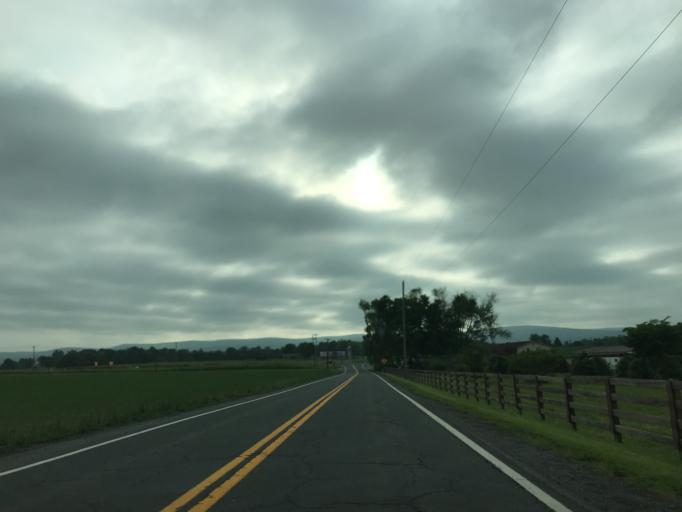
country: US
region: Maryland
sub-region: Frederick County
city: Walkersville
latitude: 39.4815
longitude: -77.3934
